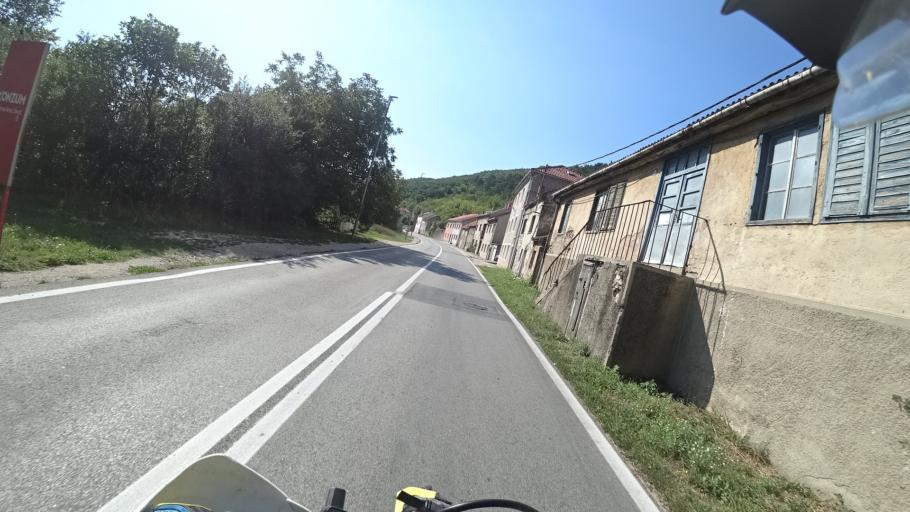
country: HR
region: Sibensko-Kniniska
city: Knin
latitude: 44.0322
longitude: 16.1895
